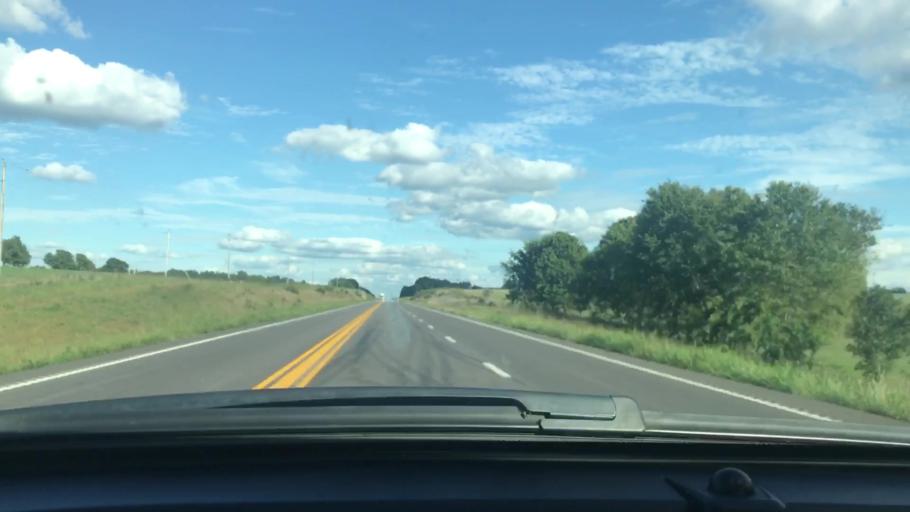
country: US
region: Missouri
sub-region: Oregon County
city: Thayer
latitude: 36.5852
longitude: -91.6235
